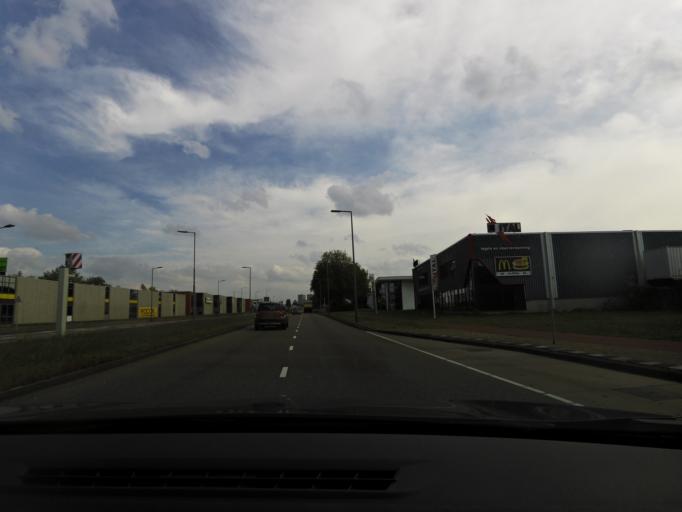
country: NL
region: South Holland
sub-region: Gemeente Schiedam
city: Schiedam
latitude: 51.9302
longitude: 4.4127
